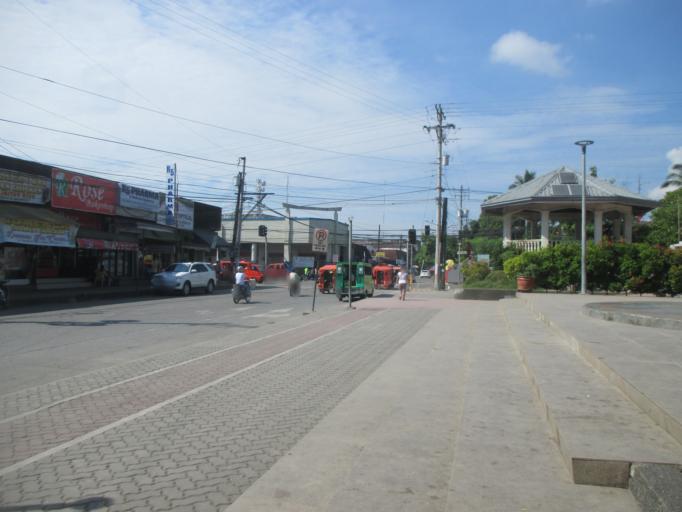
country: PH
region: Caraga
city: Butuan
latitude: 8.9478
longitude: 125.5434
